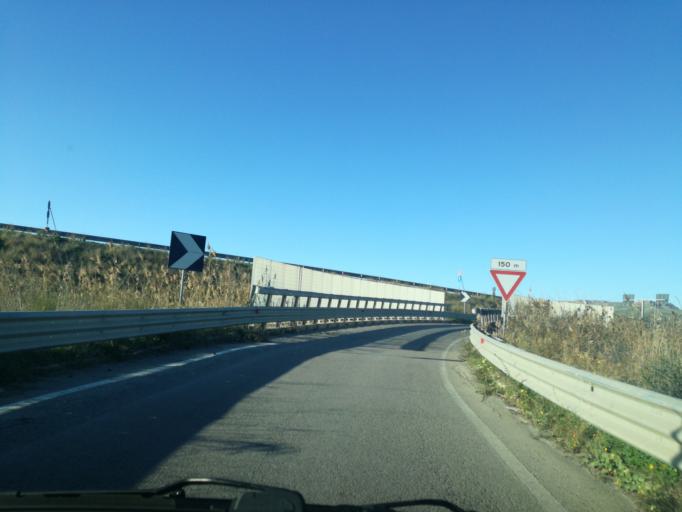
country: IT
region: Sicily
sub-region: Provincia di Caltanissetta
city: Butera
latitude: 37.1256
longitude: 14.1196
